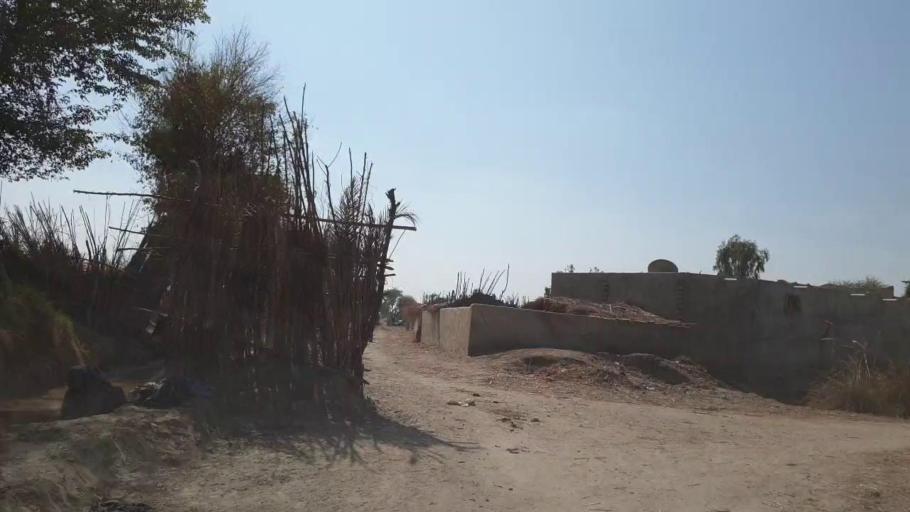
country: PK
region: Sindh
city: Mirpur Khas
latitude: 25.7355
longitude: 69.0984
